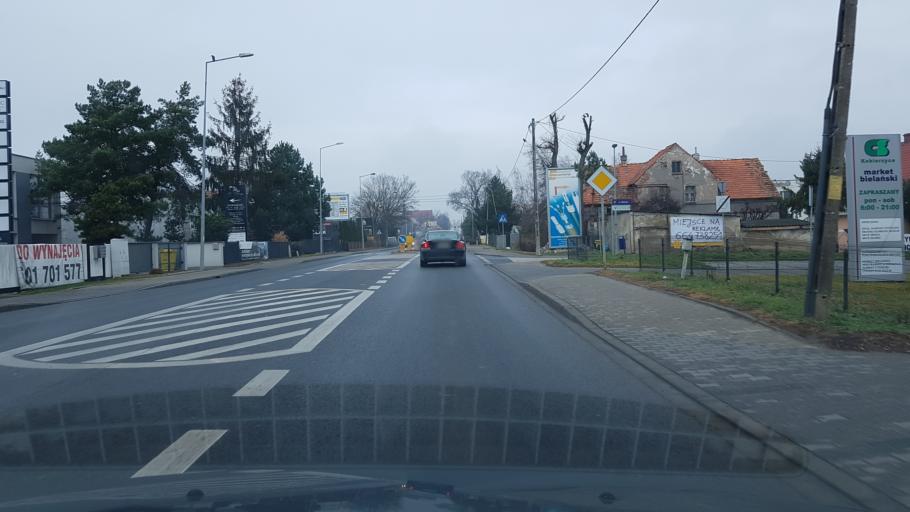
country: PL
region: Lower Silesian Voivodeship
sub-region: Powiat wroclawski
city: Bielany Wroclawskie
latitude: 51.0350
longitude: 16.9678
